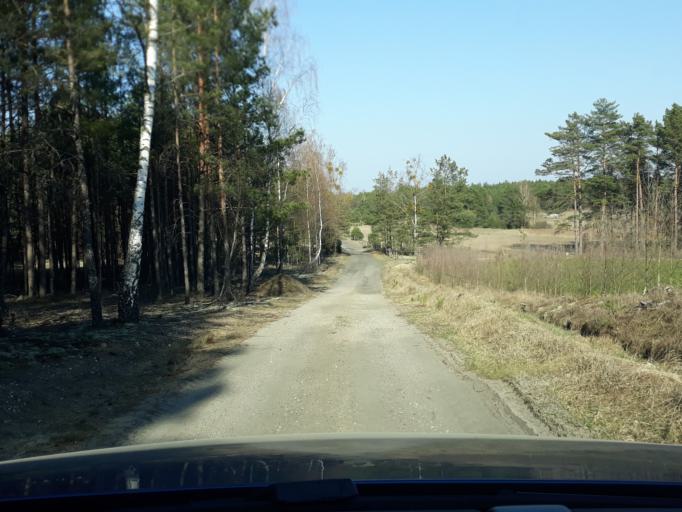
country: PL
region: Pomeranian Voivodeship
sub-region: Powiat bytowski
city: Lipnica
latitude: 53.8987
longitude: 17.4174
